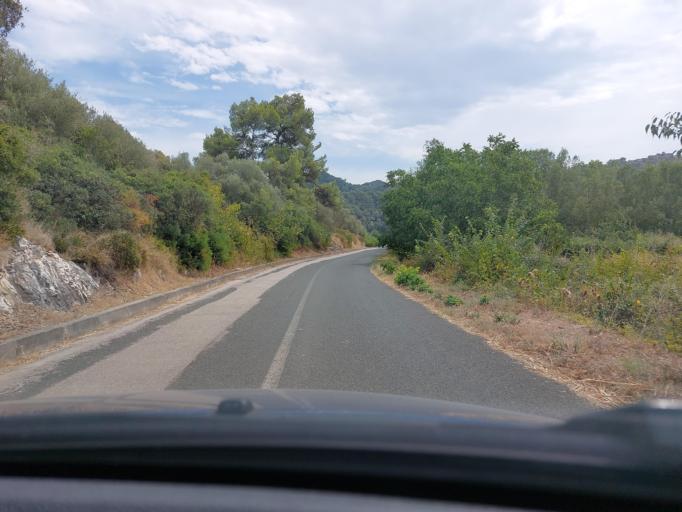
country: HR
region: Dubrovacko-Neretvanska
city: Smokvica
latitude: 42.7643
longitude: 16.8957
